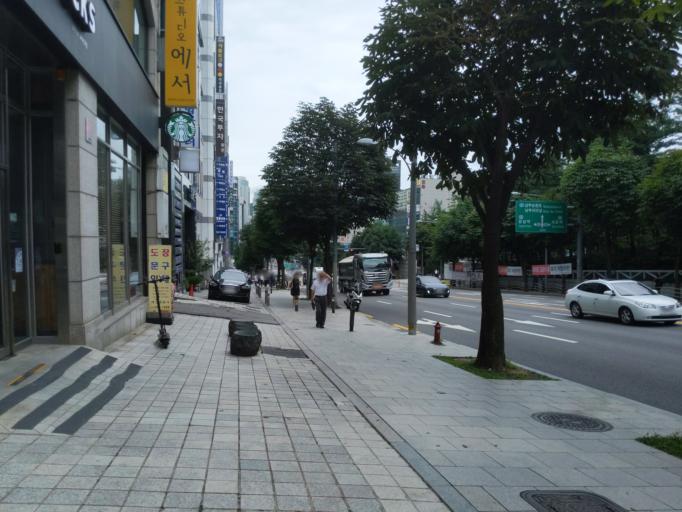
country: KR
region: Seoul
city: Seoul
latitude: 37.4965
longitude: 127.0132
